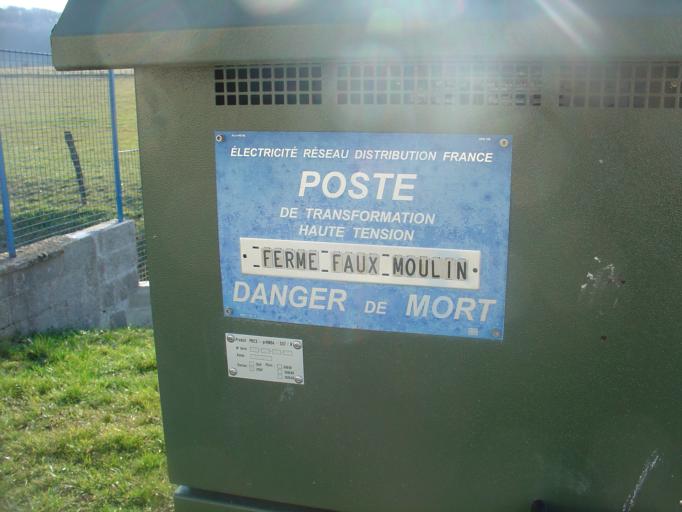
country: FR
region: Lorraine
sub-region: Departement de Meurthe-et-Moselle
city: Foug
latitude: 48.7230
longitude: 5.7972
